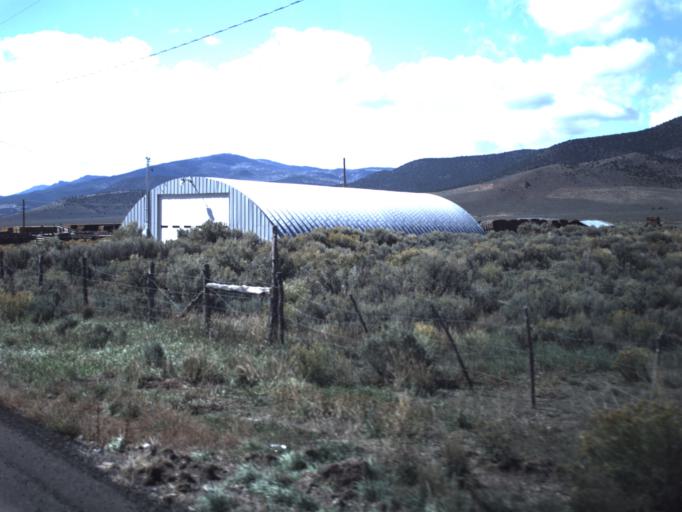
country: US
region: Utah
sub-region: Sevier County
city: Monroe
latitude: 38.4702
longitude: -111.9055
